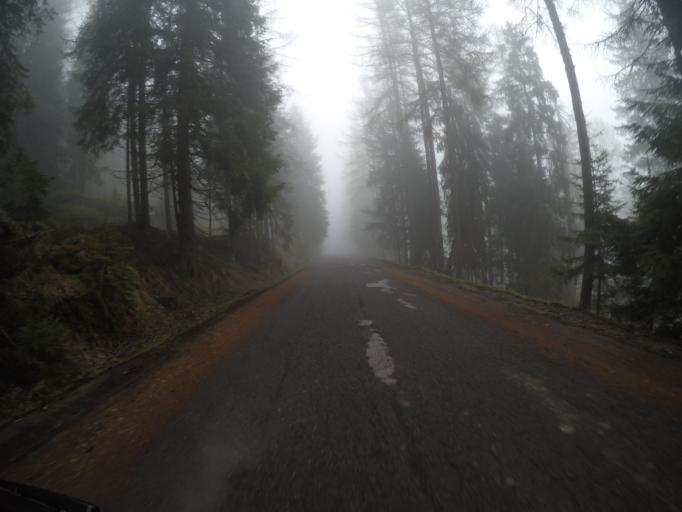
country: SK
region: Presovsky
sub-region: Okres Poprad
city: Strba
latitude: 49.1240
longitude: 20.0712
